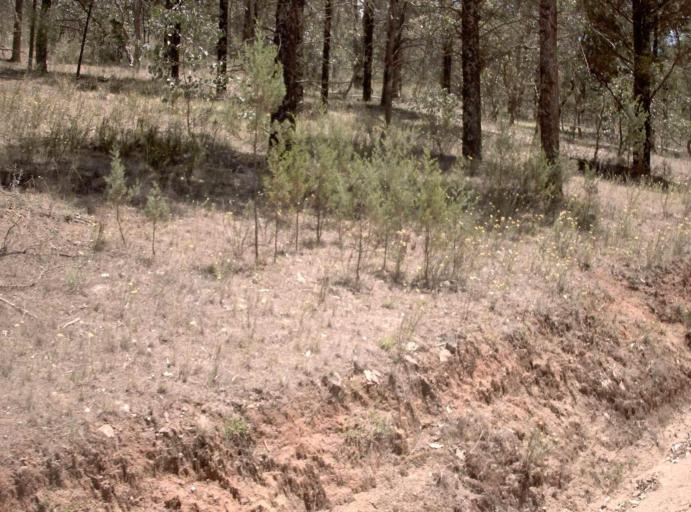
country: AU
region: New South Wales
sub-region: Snowy River
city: Jindabyne
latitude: -36.9003
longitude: 148.4179
